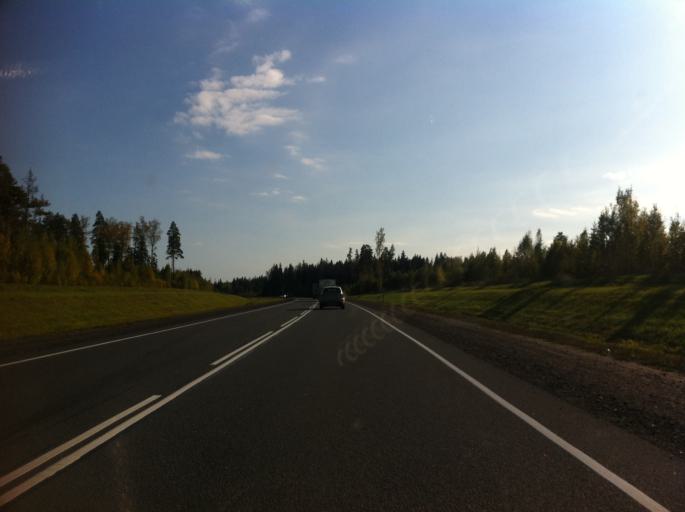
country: RU
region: Leningrad
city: Luga
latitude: 58.7651
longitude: 29.8822
